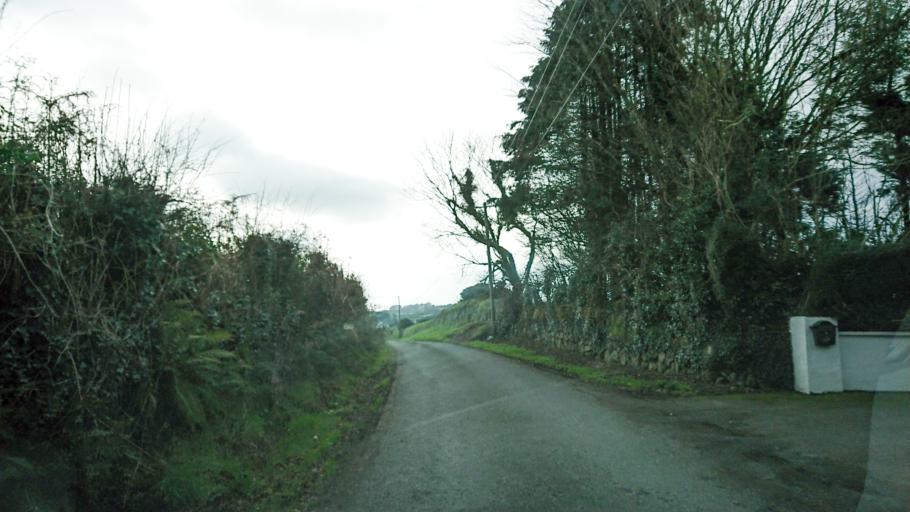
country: IE
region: Munster
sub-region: Waterford
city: Tra Mhor
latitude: 52.1905
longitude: -7.1747
